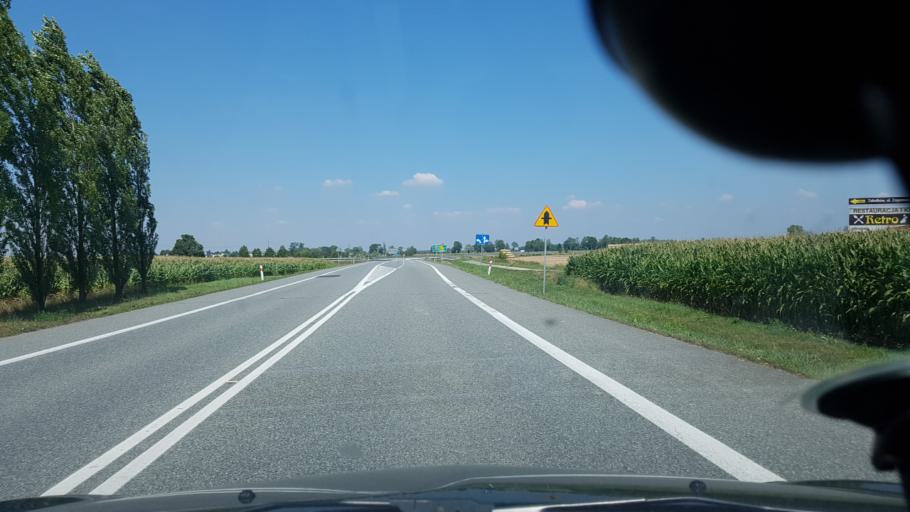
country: PL
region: Silesian Voivodeship
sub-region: Powiat wodzislawski
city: Olza
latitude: 49.9410
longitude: 18.3287
